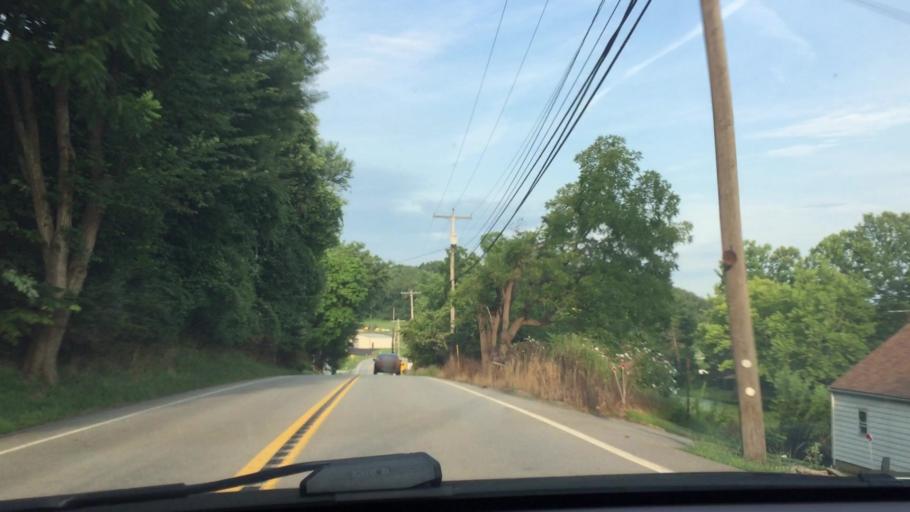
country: US
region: Pennsylvania
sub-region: Washington County
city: McMurray
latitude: 40.1790
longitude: -80.1123
